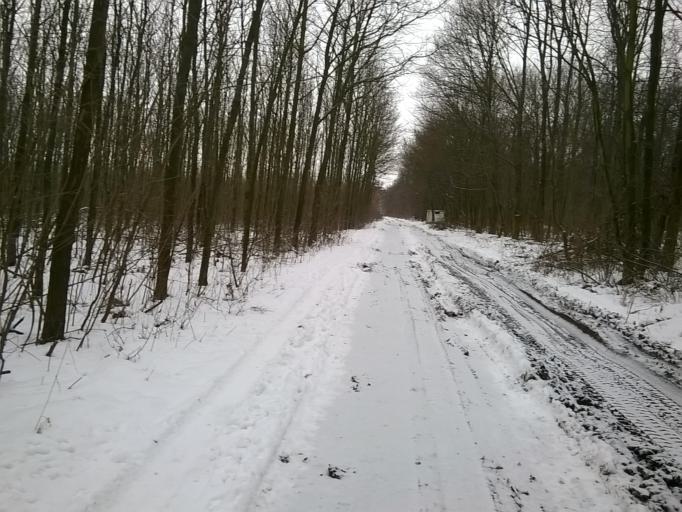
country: SK
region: Nitriansky
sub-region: Okres Nitra
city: Nitra
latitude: 48.2795
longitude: 18.0138
